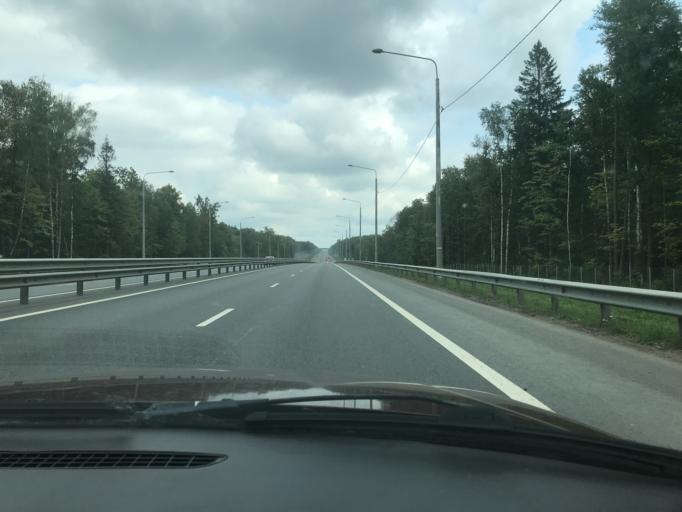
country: RU
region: Kaluga
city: Mstikhino
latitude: 54.5913
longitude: 36.0817
